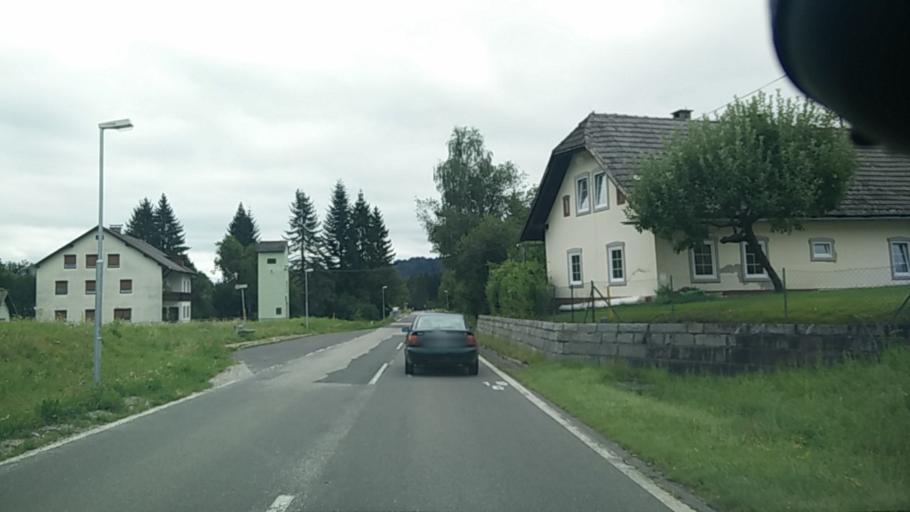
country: AT
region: Carinthia
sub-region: Politischer Bezirk Villach Land
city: Rosegg
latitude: 46.5526
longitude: 13.9913
